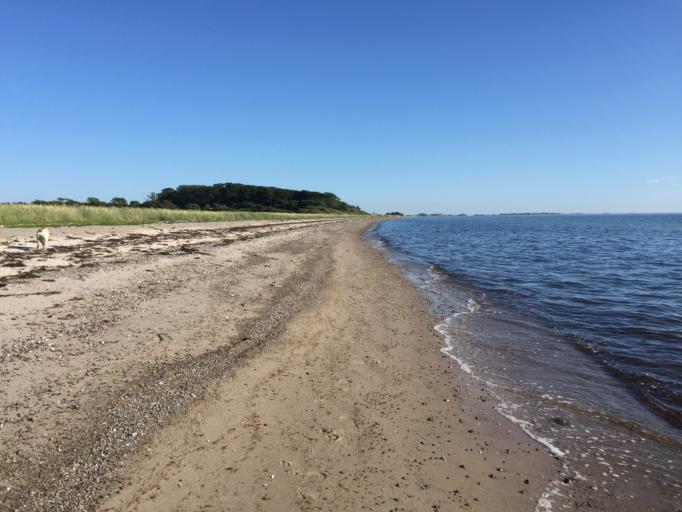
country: DK
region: Zealand
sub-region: Slagelse Kommune
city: Korsor
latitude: 55.2275
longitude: 11.1715
